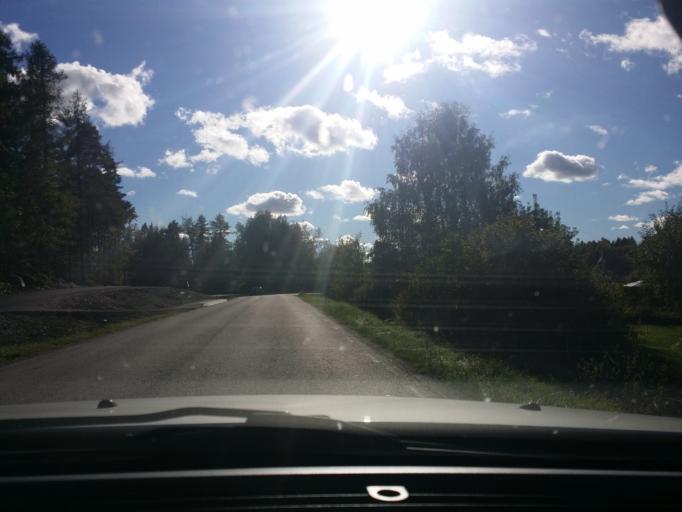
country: SE
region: Vaestmanland
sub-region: Vasteras
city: Vasteras
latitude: 59.5785
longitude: 16.4903
